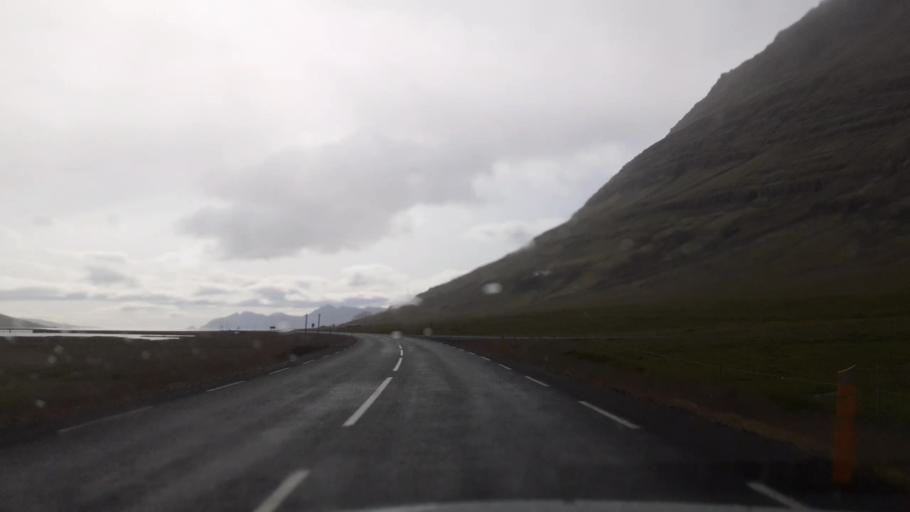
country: IS
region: East
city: Eskifjoerdur
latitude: 65.0789
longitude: -14.0524
